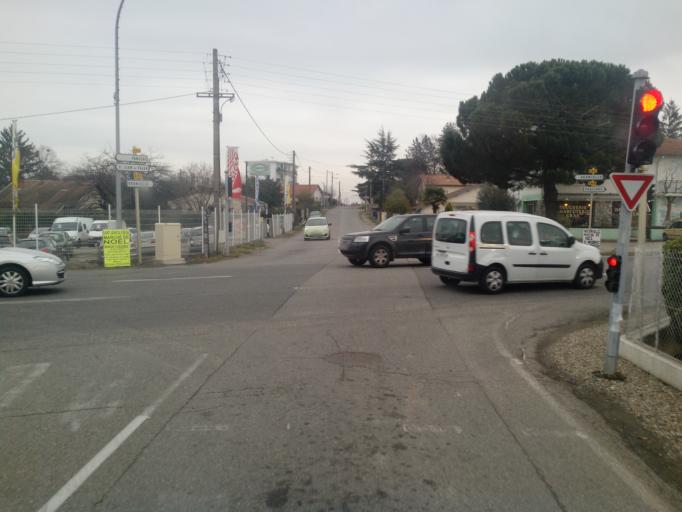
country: FR
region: Midi-Pyrenees
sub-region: Departement de l'Ariege
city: Saint-Jean-du-Falga
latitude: 43.0819
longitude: 1.6294
